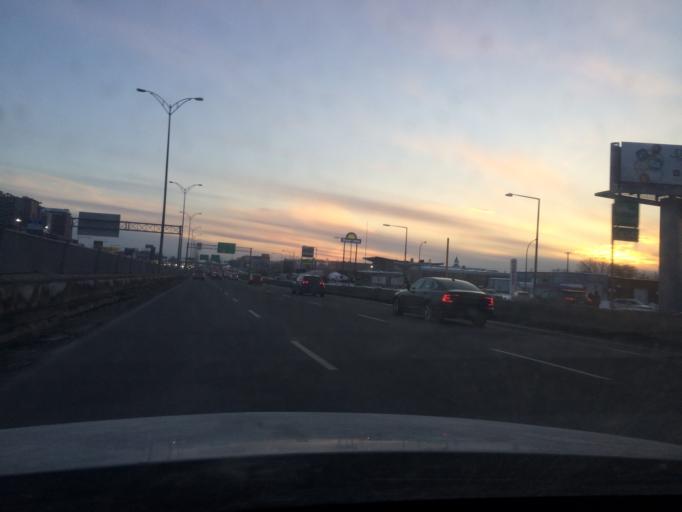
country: CA
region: Quebec
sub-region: Montreal
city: Saint-Leonard
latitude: 45.5894
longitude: -73.5826
